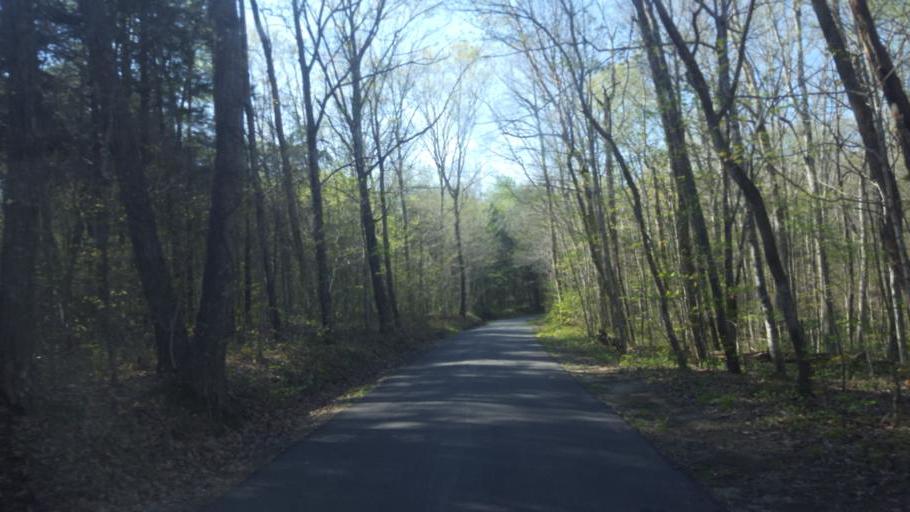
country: US
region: Kentucky
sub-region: Barren County
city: Cave City
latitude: 37.1874
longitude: -86.0487
